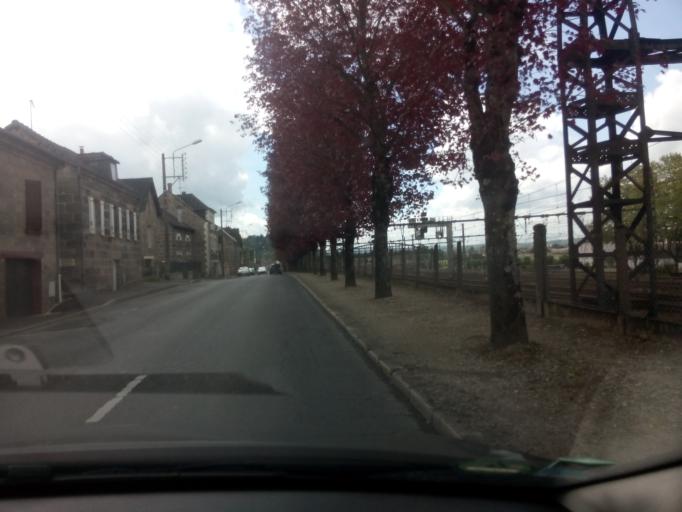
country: FR
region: Limousin
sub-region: Departement de la Correze
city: Brive-la-Gaillarde
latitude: 45.1524
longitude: 1.5186
